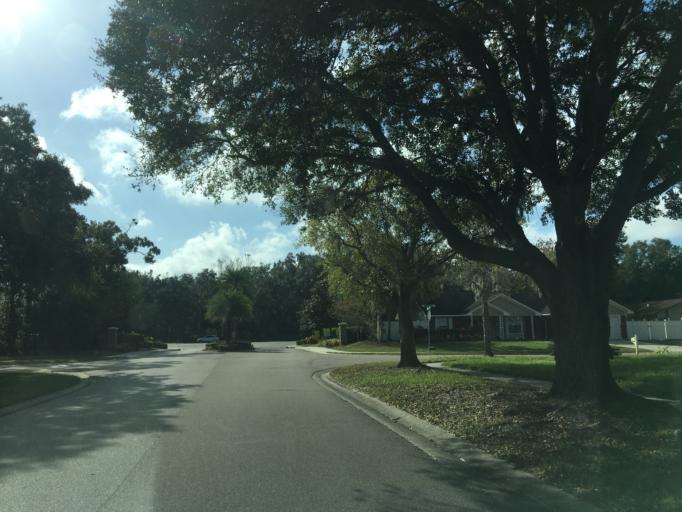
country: US
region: Florida
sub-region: Orange County
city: Azalea Park
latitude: 28.5110
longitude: -81.2761
